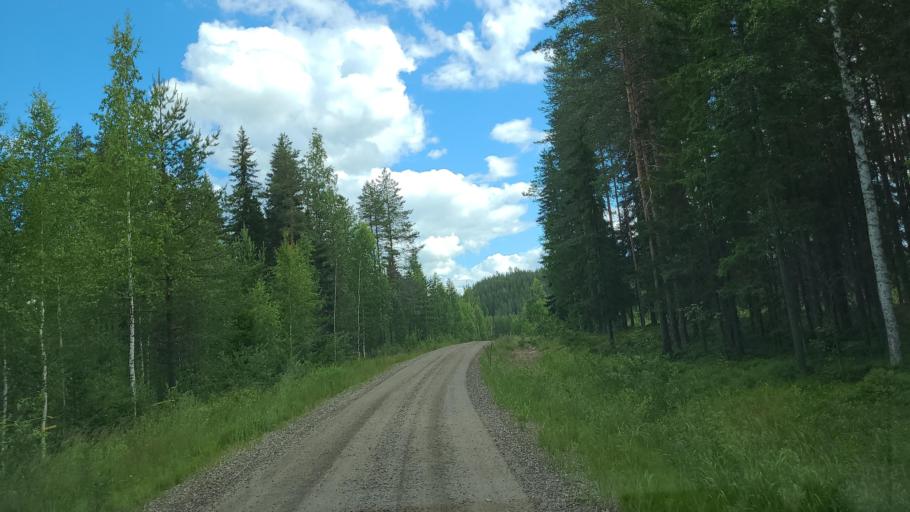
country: FI
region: Northern Savo
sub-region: Koillis-Savo
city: Kaavi
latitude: 63.0395
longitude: 28.8042
